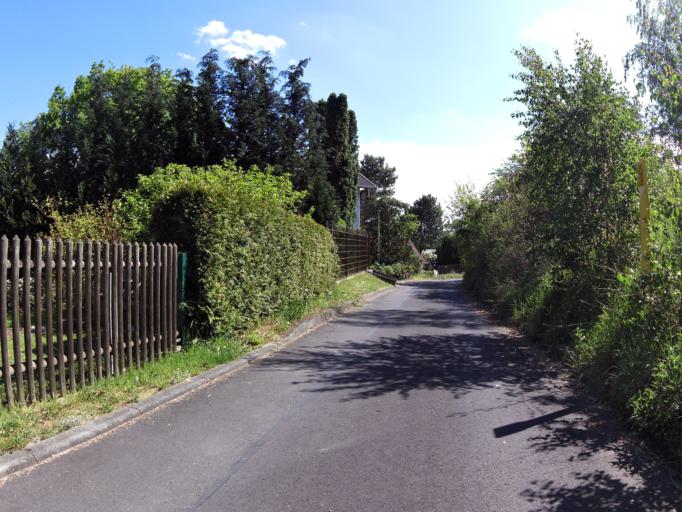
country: DE
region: Thuringia
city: Leimbach
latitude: 50.8085
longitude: 10.2099
